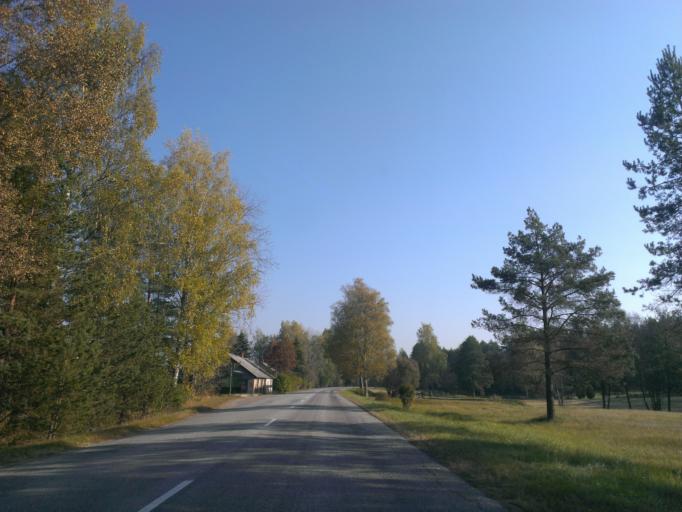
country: LV
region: Garkalne
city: Garkalne
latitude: 57.0129
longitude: 24.4590
